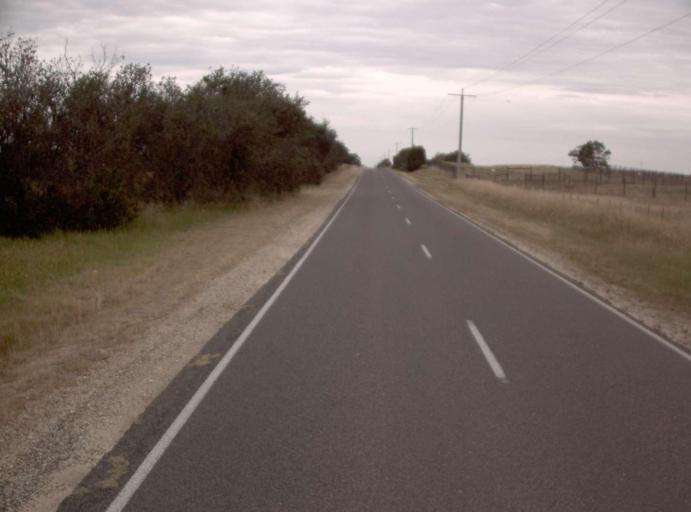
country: AU
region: Victoria
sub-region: Wellington
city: Sale
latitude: -38.1809
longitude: 147.2409
